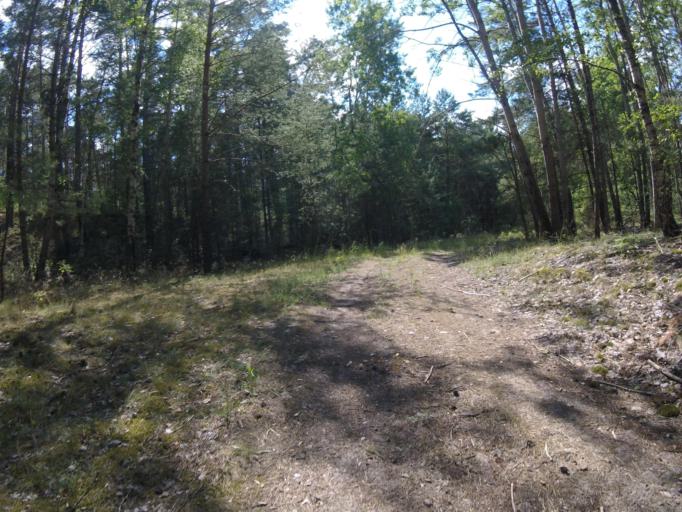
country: DE
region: Brandenburg
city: Wildau
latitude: 52.3275
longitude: 13.6728
